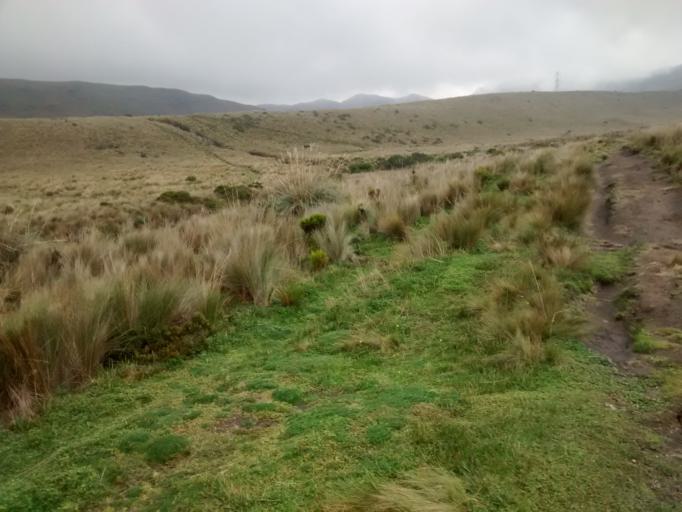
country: EC
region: Pichincha
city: Quito
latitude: -0.1818
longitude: -78.5426
